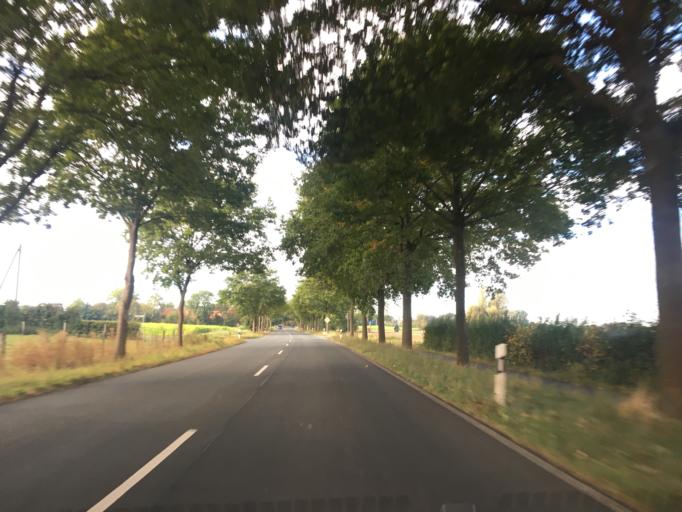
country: DE
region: North Rhine-Westphalia
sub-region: Regierungsbezirk Munster
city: Altenberge
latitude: 51.9981
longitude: 7.5042
